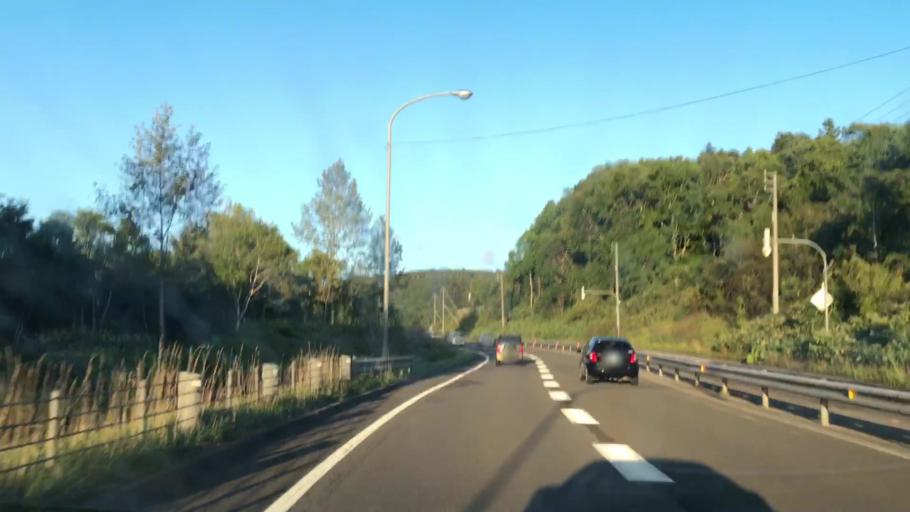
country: JP
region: Hokkaido
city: Sapporo
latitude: 42.8526
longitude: 141.0763
